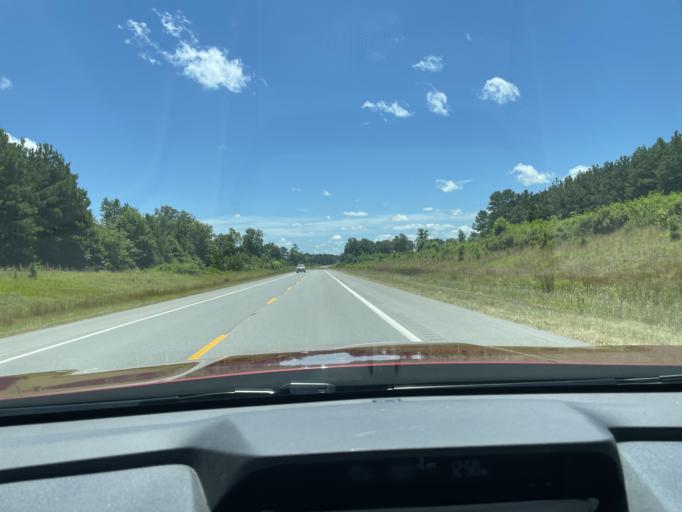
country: US
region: Arkansas
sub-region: Lincoln County
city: Star City
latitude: 33.9430
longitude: -91.8963
